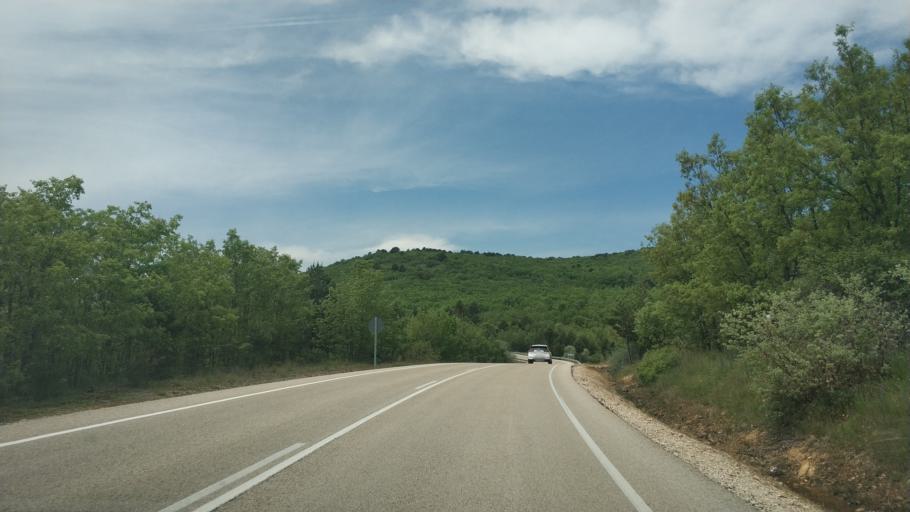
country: ES
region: Castille and Leon
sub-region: Provincia de Soria
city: Vinuesa
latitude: 41.8867
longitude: -2.7002
